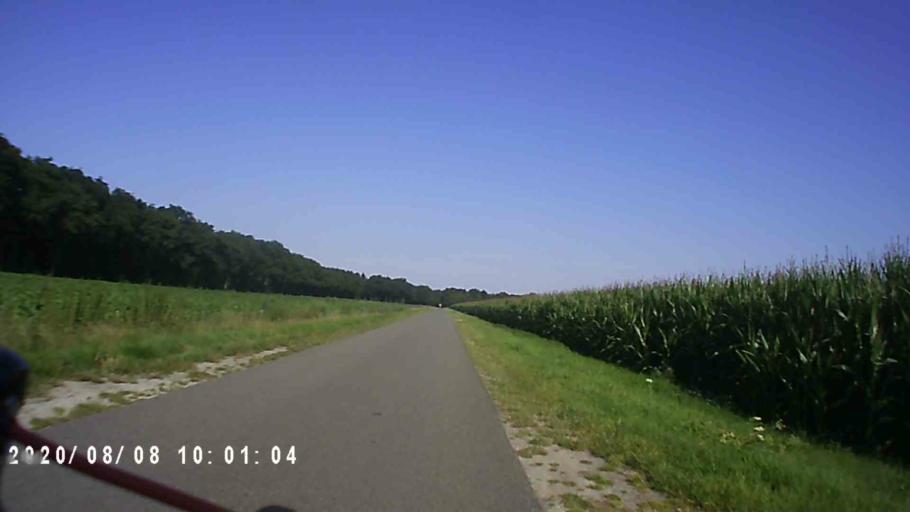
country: NL
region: Groningen
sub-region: Gemeente Leek
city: Leek
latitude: 53.1040
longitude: 6.3928
